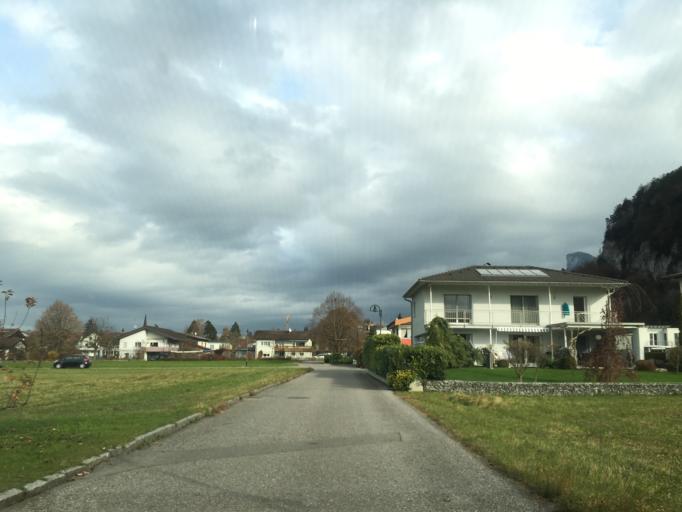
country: AT
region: Vorarlberg
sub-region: Politischer Bezirk Feldkirch
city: Gotzis
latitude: 47.3257
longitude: 9.6357
